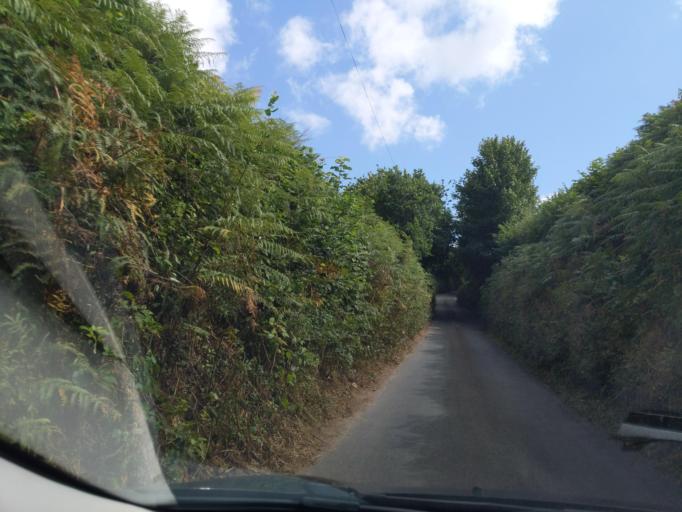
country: GB
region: England
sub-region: Devon
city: Modbury
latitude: 50.3582
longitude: -3.8908
